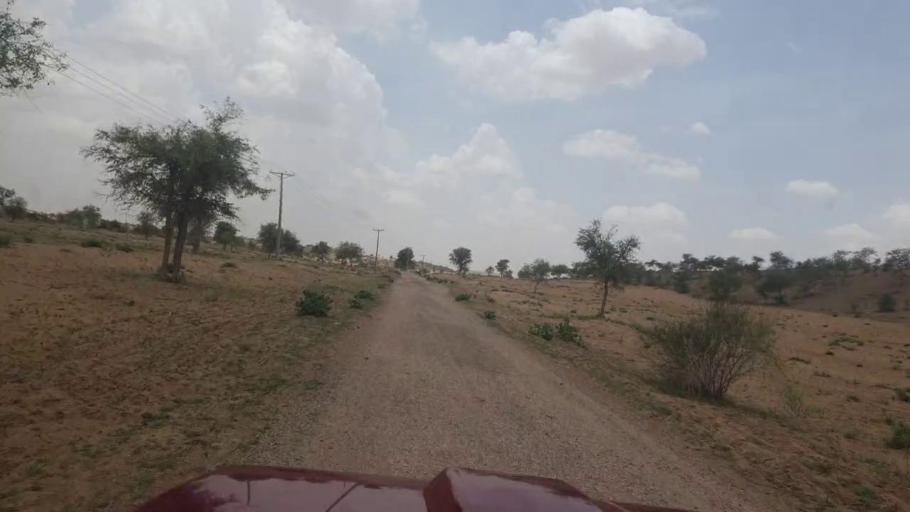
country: PK
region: Sindh
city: Islamkot
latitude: 25.2101
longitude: 70.4533
